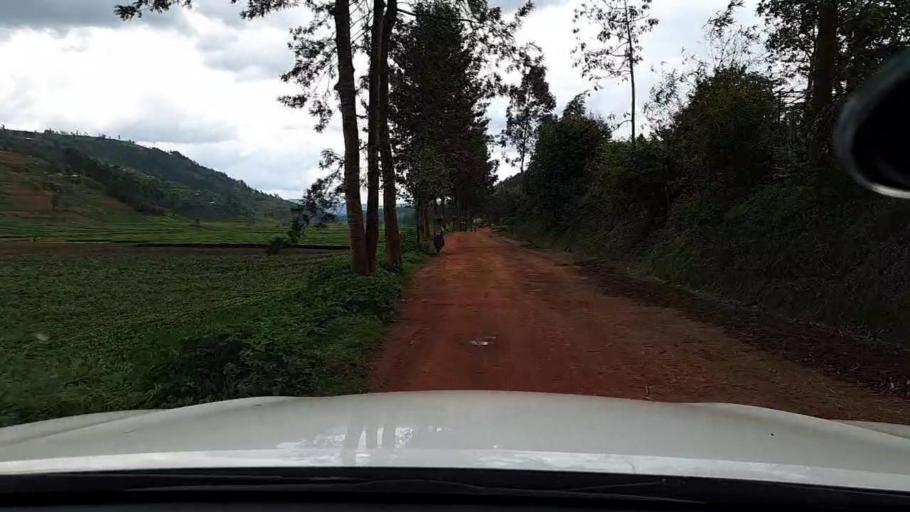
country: RW
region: Northern Province
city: Byumba
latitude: -1.6679
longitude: 29.9224
